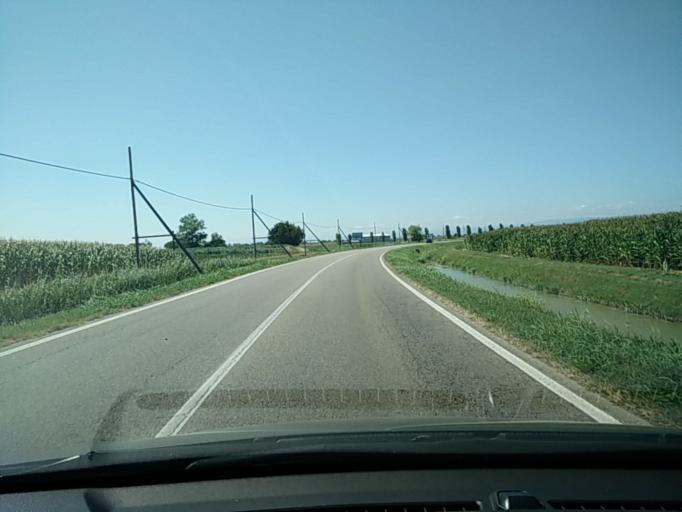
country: IT
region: Veneto
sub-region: Provincia di Venezia
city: La Salute di Livenza
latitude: 45.6377
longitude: 12.8474
